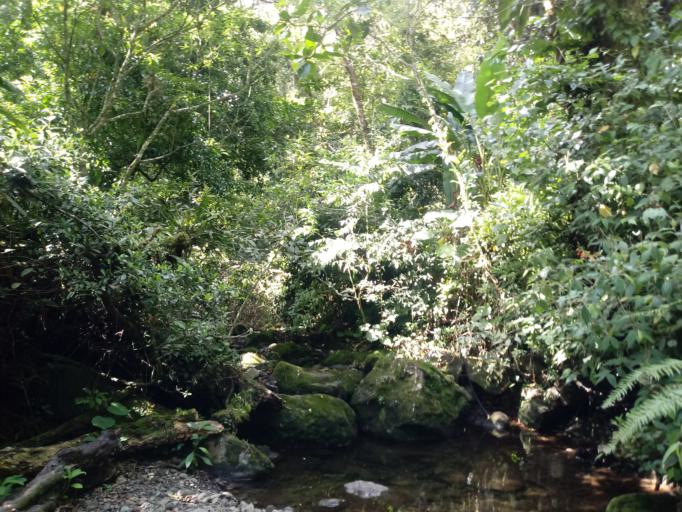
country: CR
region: Heredia
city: Angeles
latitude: 10.0411
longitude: -84.0422
